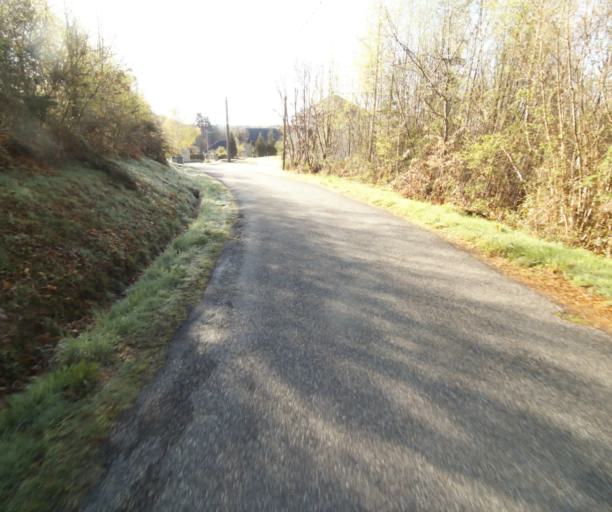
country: FR
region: Limousin
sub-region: Departement de la Correze
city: Laguenne
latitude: 45.2756
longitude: 1.8634
